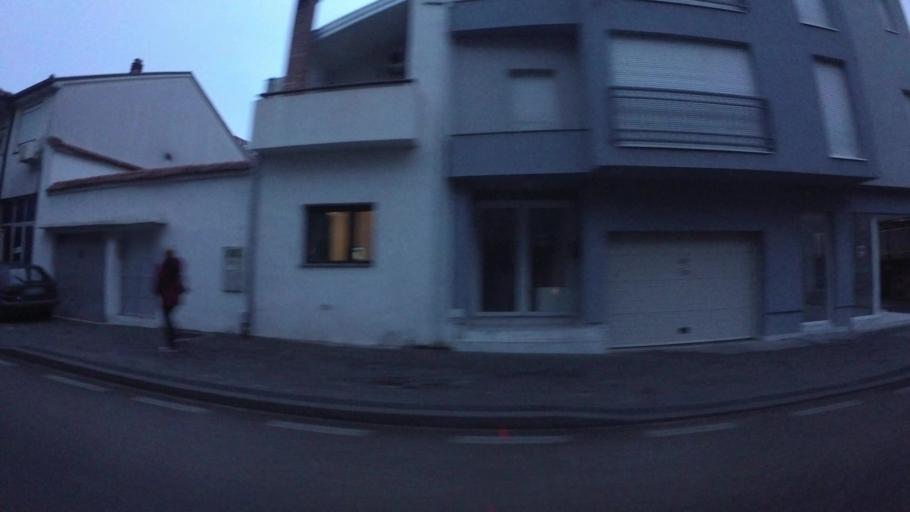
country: BA
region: Federation of Bosnia and Herzegovina
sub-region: Hercegovacko-Bosanski Kanton
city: Mostar
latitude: 43.3331
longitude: 17.8180
